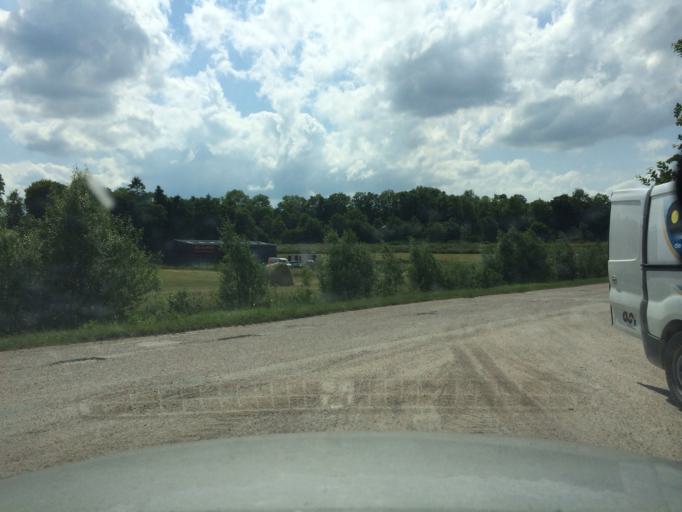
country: FR
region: Lorraine
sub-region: Departement de la Meuse
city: Vacon
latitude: 48.6866
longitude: 5.6332
